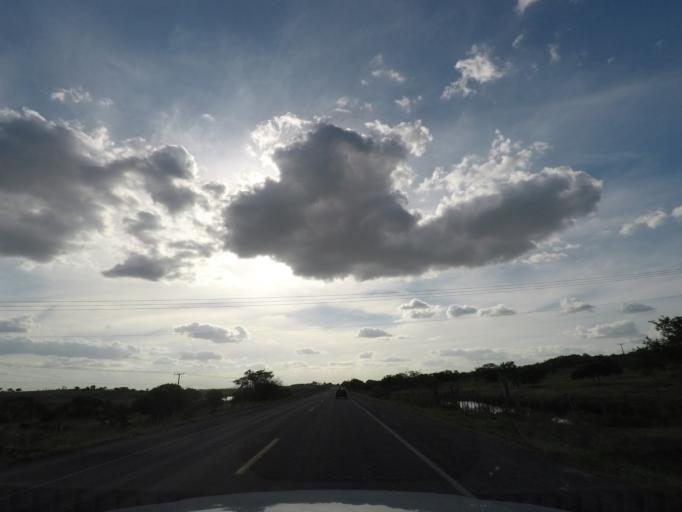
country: BR
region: Bahia
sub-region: Anguera
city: Anguera
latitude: -12.1856
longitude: -39.4807
